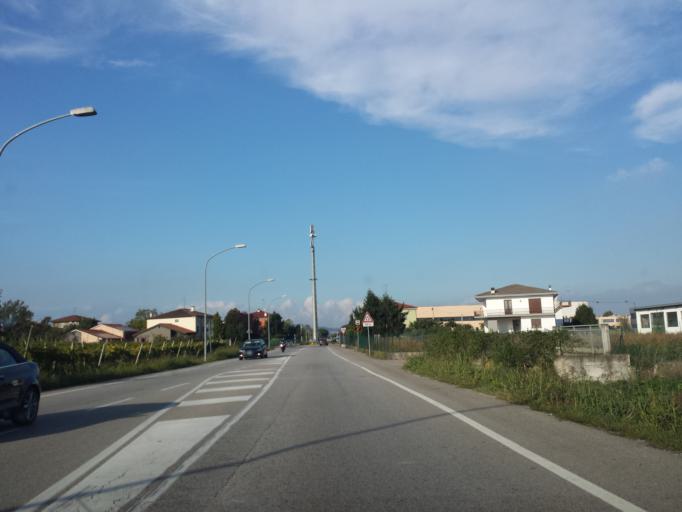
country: IT
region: Veneto
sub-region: Provincia di Vicenza
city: Brendola
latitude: 45.4942
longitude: 11.4413
